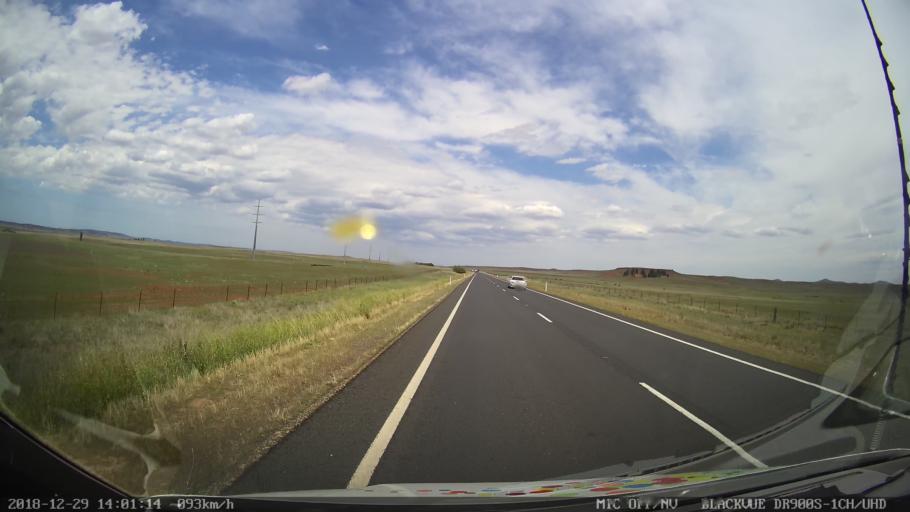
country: AU
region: New South Wales
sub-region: Cooma-Monaro
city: Cooma
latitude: -36.2728
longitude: 149.1668
